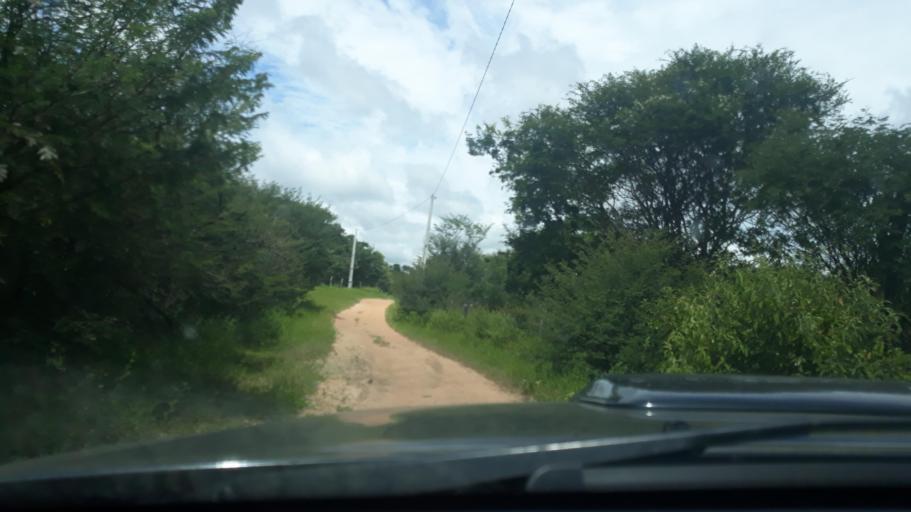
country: BR
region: Bahia
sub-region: Riacho De Santana
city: Riacho de Santana
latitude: -13.8619
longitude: -43.0722
